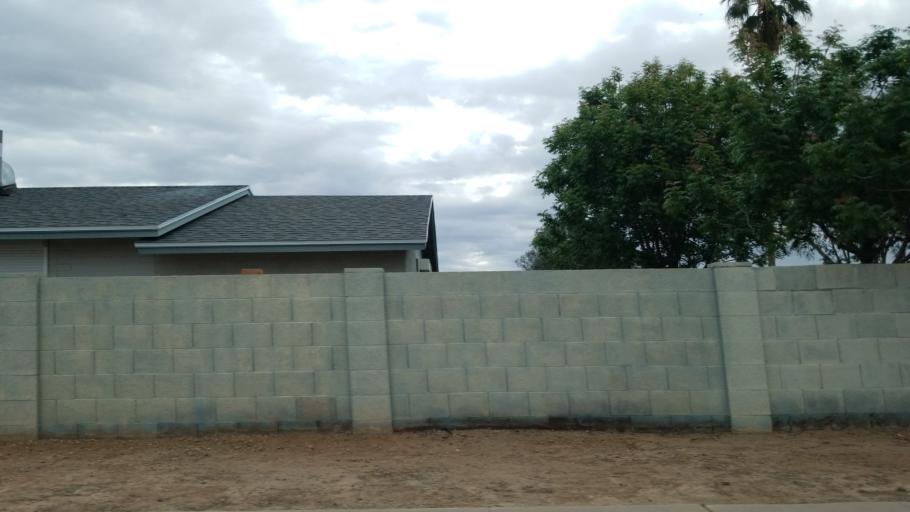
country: US
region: Arizona
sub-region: Maricopa County
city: Paradise Valley
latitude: 33.5973
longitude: -112.0305
